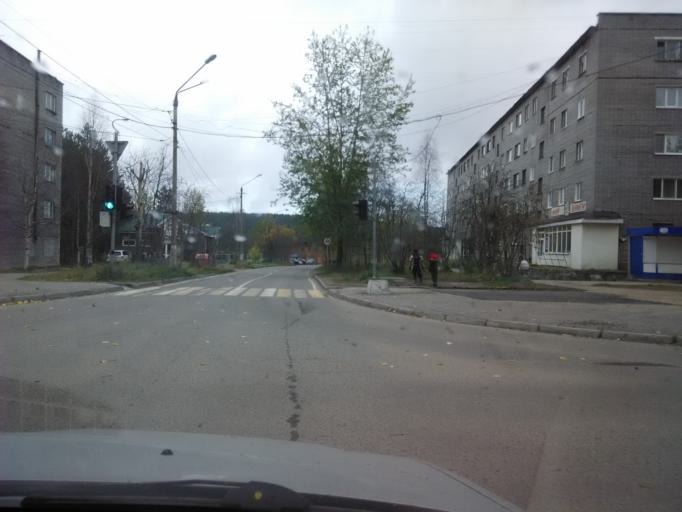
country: RU
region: Murmansk
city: Polyarnyye Zori
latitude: 67.3700
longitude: 32.5050
